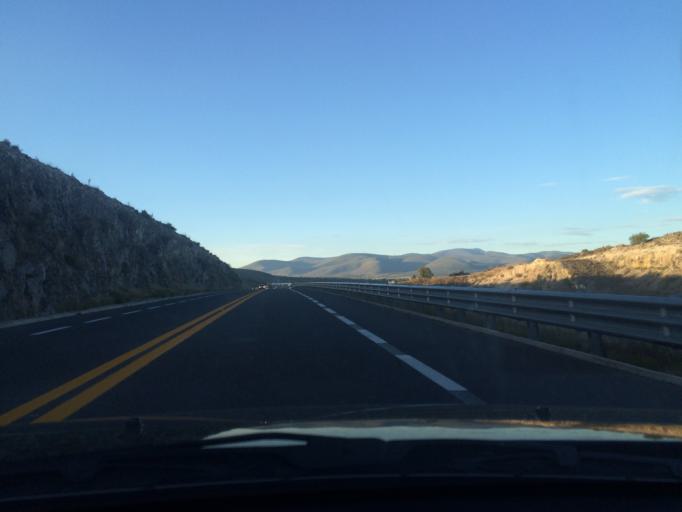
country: MX
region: Puebla
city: Cuacnopalan
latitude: 18.8043
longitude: -97.4901
